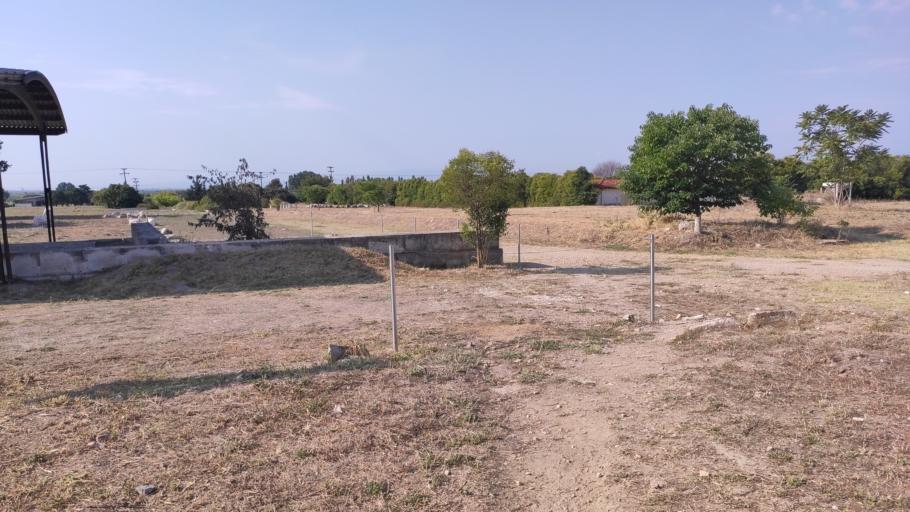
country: GR
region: Central Macedonia
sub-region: Nomos Pellis
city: Pella
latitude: 40.7548
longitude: 22.5175
